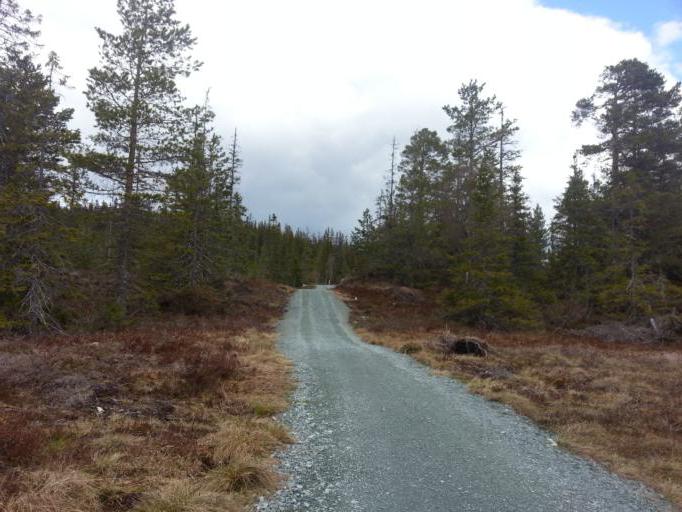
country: NO
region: Nord-Trondelag
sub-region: Levanger
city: Skogn
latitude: 63.5859
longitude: 11.0884
